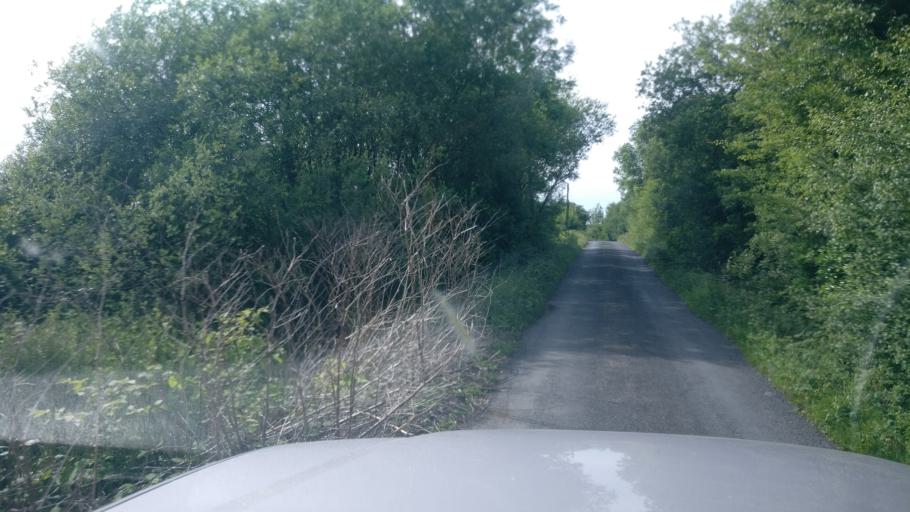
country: IE
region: Connaught
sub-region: County Galway
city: Gort
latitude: 53.0980
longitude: -8.6975
